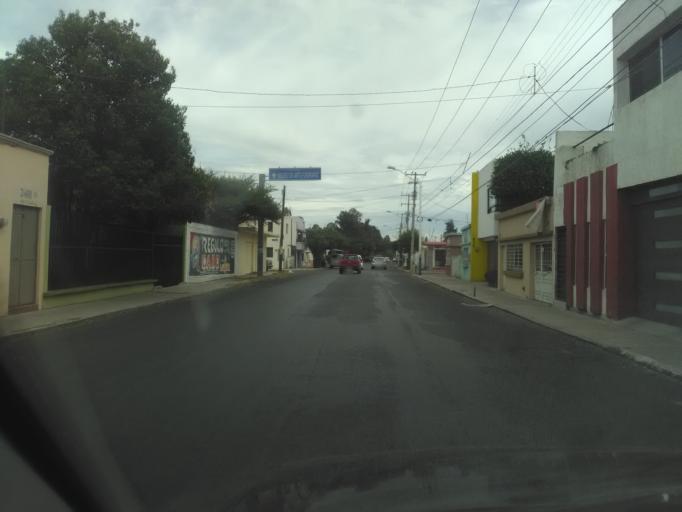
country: MX
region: Durango
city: Victoria de Durango
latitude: 24.0262
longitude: -104.6441
